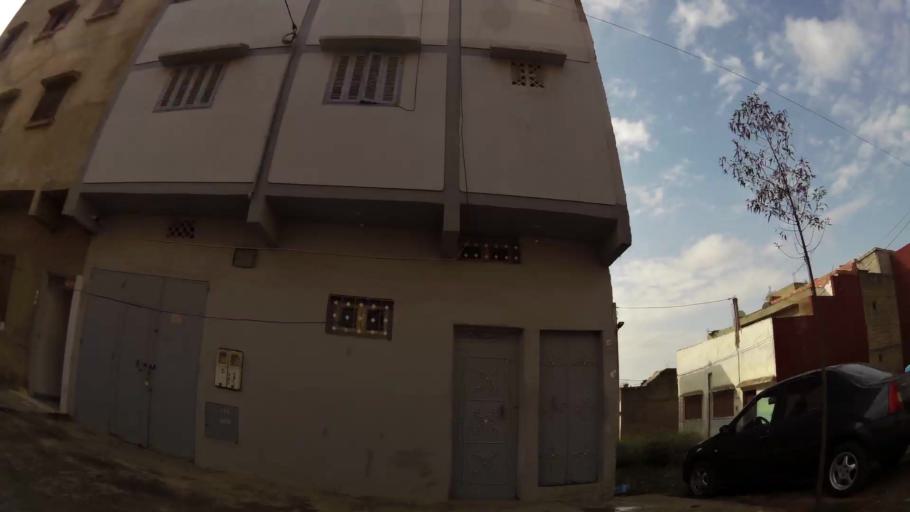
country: MA
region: Rabat-Sale-Zemmour-Zaer
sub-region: Khemisset
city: Tiflet
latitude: 33.8859
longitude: -6.3115
